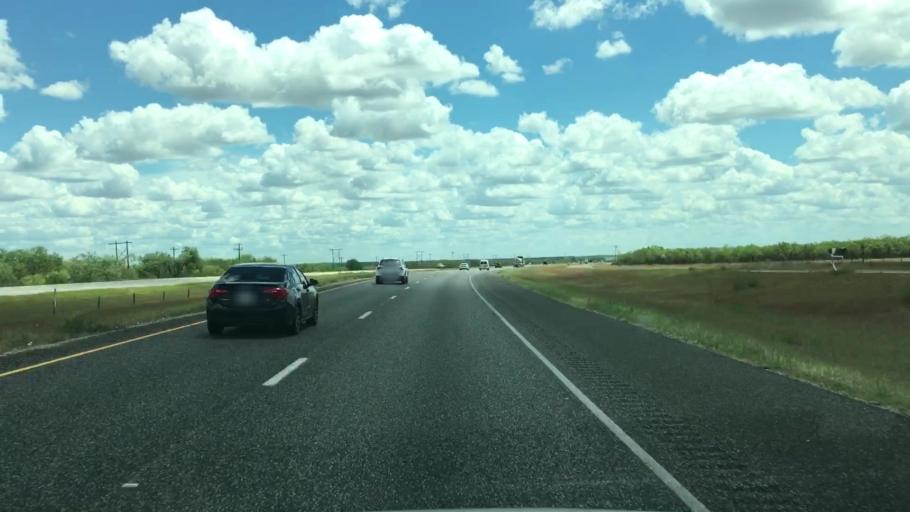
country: US
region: Texas
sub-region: Atascosa County
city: Pleasanton
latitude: 28.8690
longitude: -98.3932
